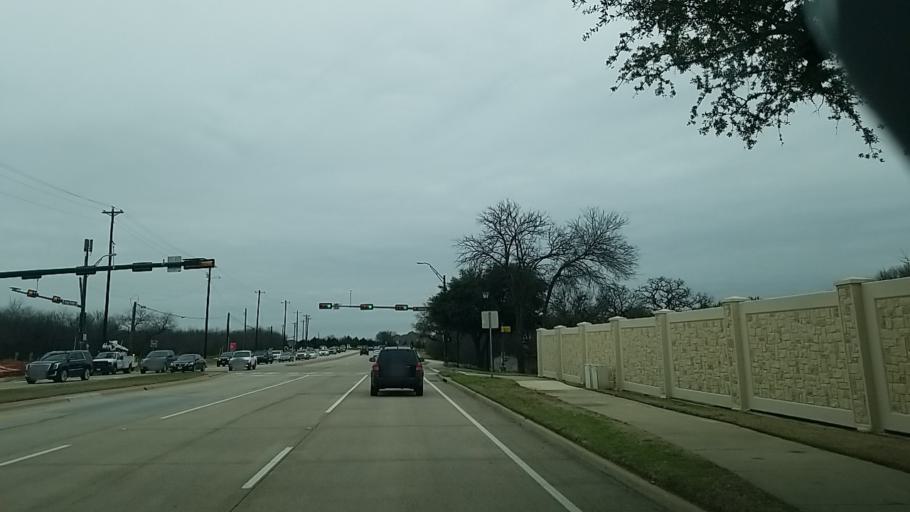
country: US
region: Texas
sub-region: Denton County
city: Flower Mound
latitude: 33.0035
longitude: -97.0706
